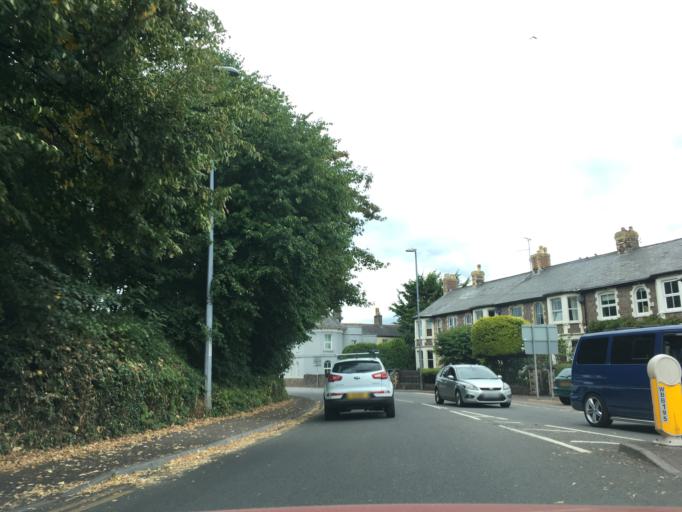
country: GB
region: Wales
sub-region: Monmouthshire
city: Abergavenny
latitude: 51.8250
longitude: -3.0275
